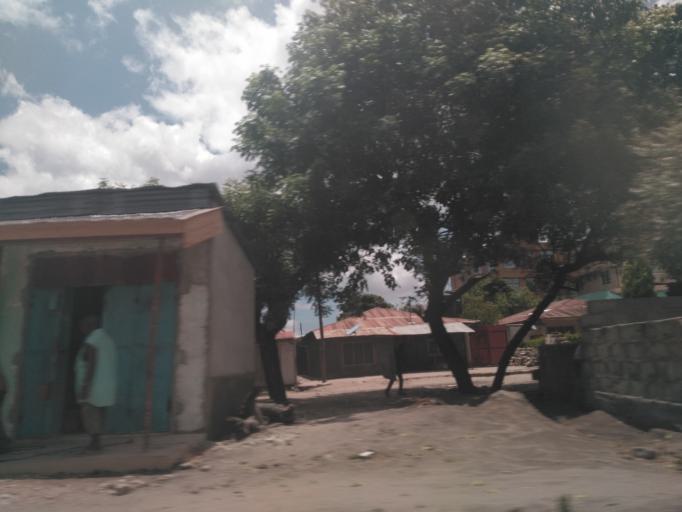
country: TZ
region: Dar es Salaam
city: Dar es Salaam
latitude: -6.8610
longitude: 39.2680
